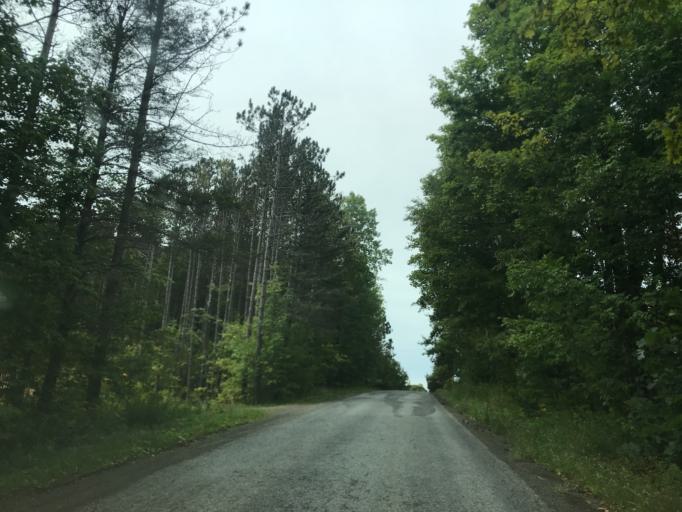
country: US
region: New York
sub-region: Otsego County
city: Worcester
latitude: 42.5950
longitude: -74.6854
